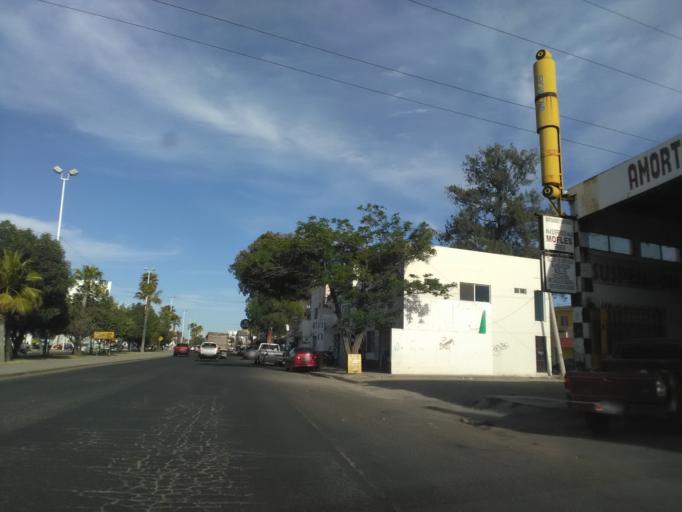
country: MX
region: Durango
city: Victoria de Durango
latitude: 24.0325
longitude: -104.6340
